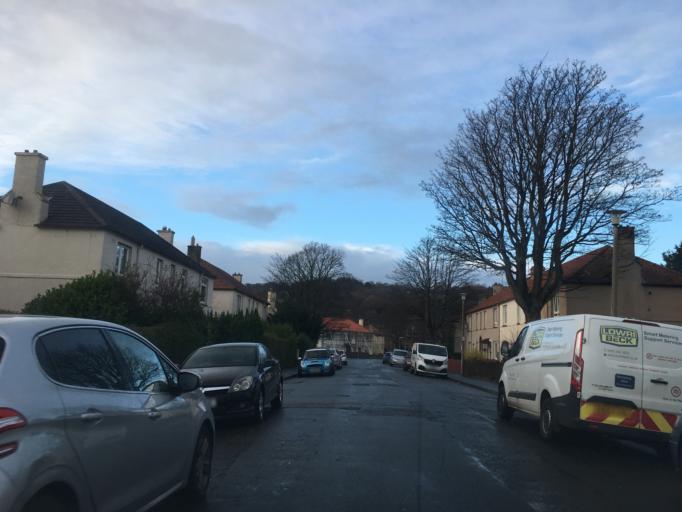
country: GB
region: Scotland
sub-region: Edinburgh
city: Colinton
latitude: 55.9414
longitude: -3.2536
